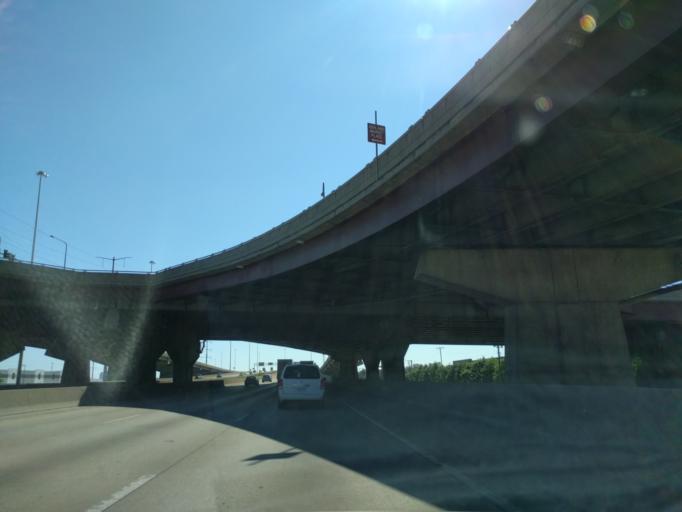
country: US
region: Illinois
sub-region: Cook County
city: Chicago
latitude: 41.8370
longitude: -87.6763
